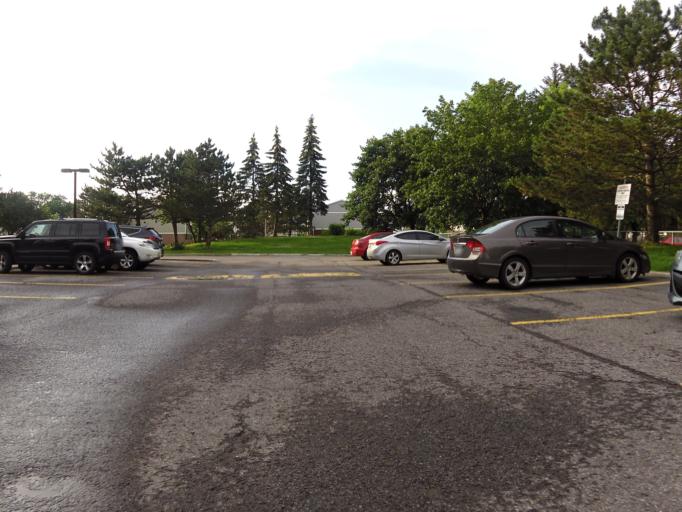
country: CA
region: Ontario
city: Bells Corners
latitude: 45.3356
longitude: -75.7461
